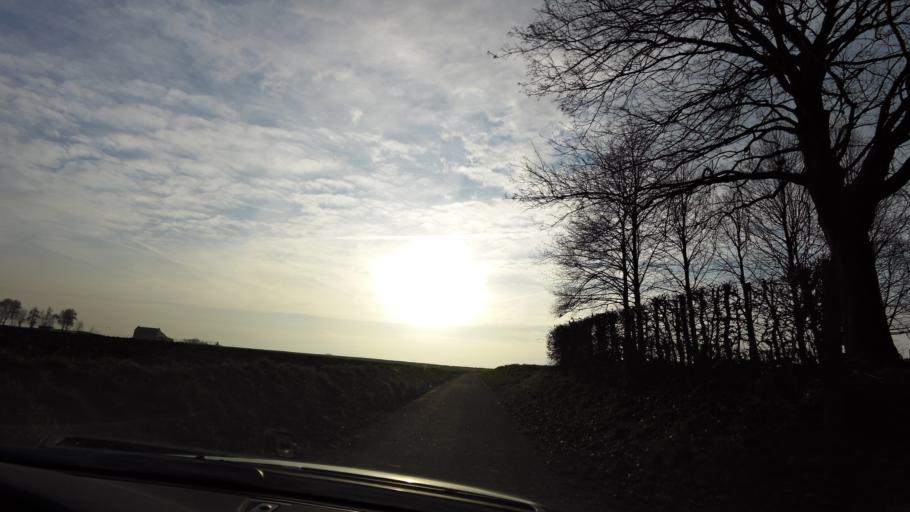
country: NL
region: Limburg
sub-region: Valkenburg aan de Geul
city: Broekhem
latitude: 50.9057
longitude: 5.8297
